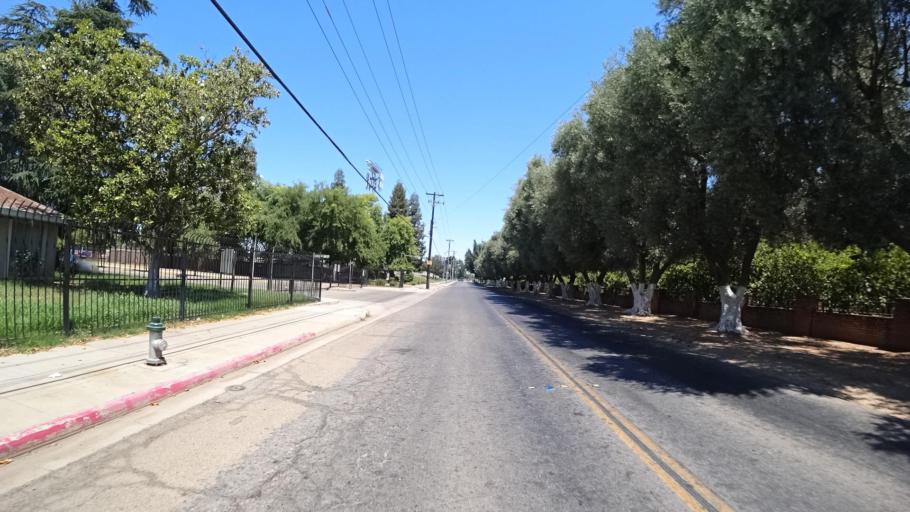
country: US
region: California
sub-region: Fresno County
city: Sunnyside
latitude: 36.7235
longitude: -119.7275
